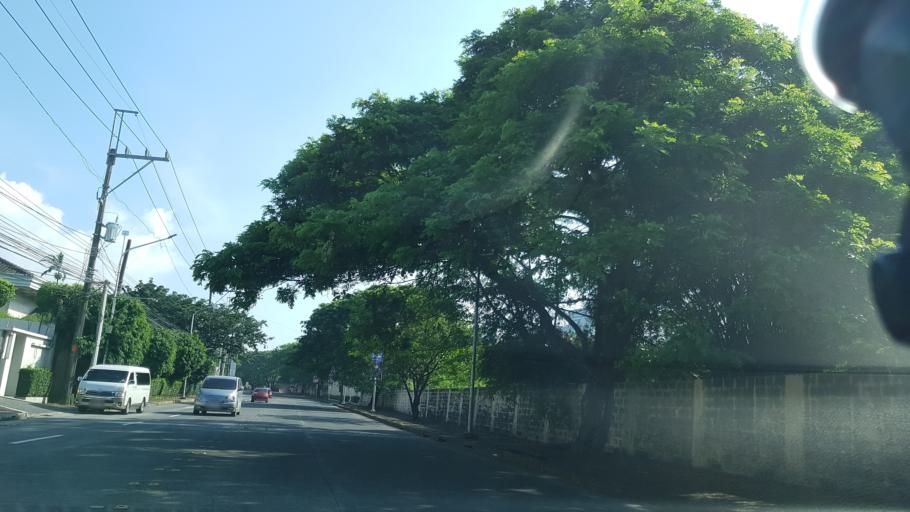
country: PH
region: Metro Manila
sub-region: Pasig
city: Pasig City
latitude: 14.5950
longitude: 121.0724
